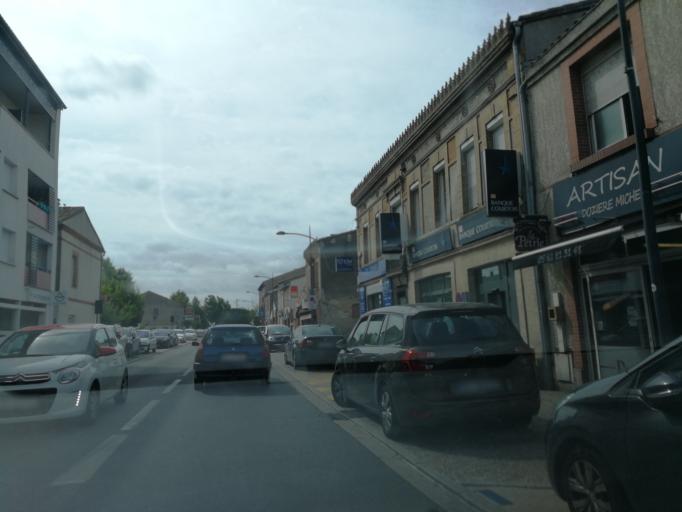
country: FR
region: Midi-Pyrenees
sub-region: Departement de la Haute-Garonne
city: Aucamville
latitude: 43.6634
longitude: 1.4308
